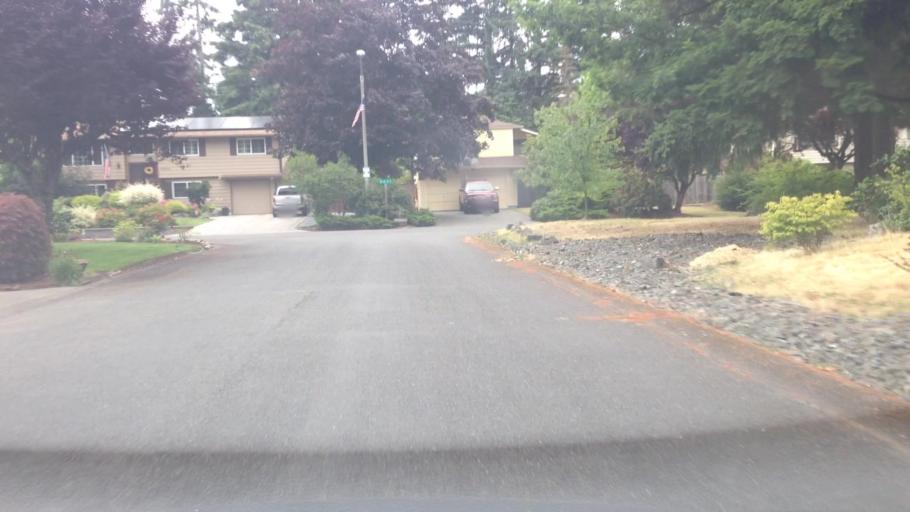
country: US
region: Washington
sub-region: Pierce County
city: South Hill
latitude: 47.1074
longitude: -122.3003
